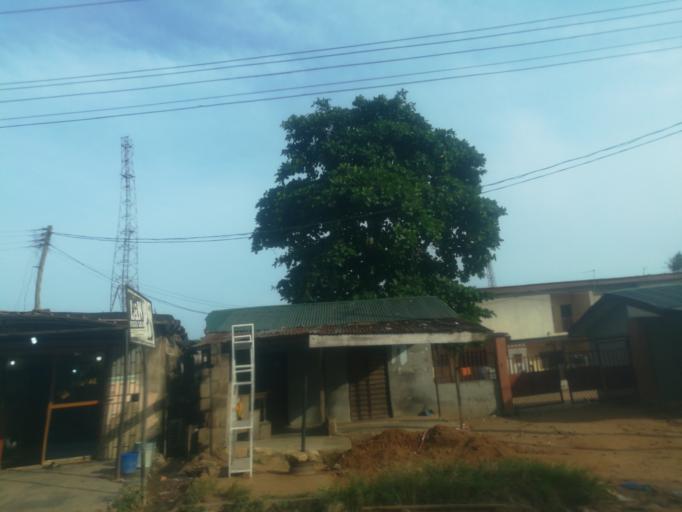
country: NG
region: Ogun
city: Abeokuta
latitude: 7.1259
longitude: 3.3244
